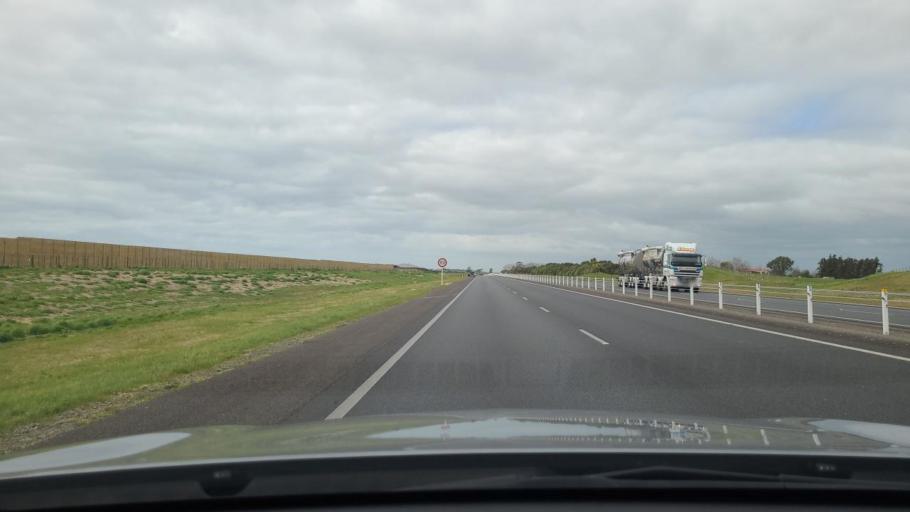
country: NZ
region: Bay of Plenty
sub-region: Western Bay of Plenty District
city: Maketu
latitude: -37.7270
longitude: 176.3282
